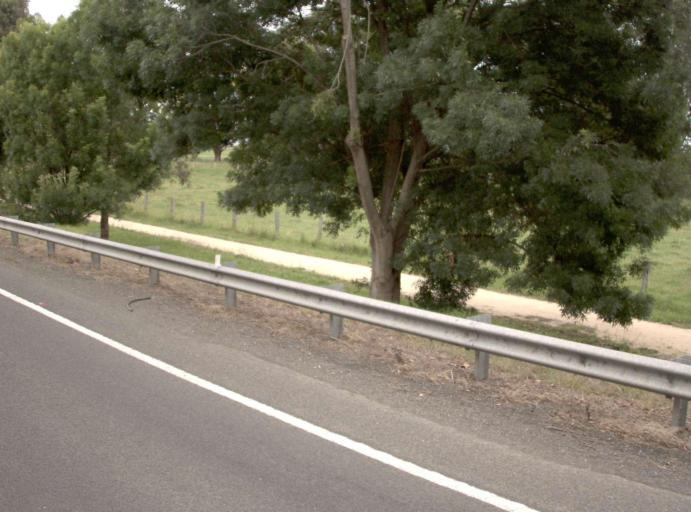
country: AU
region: Victoria
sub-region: Wellington
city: Sale
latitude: -37.9745
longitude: 147.0751
